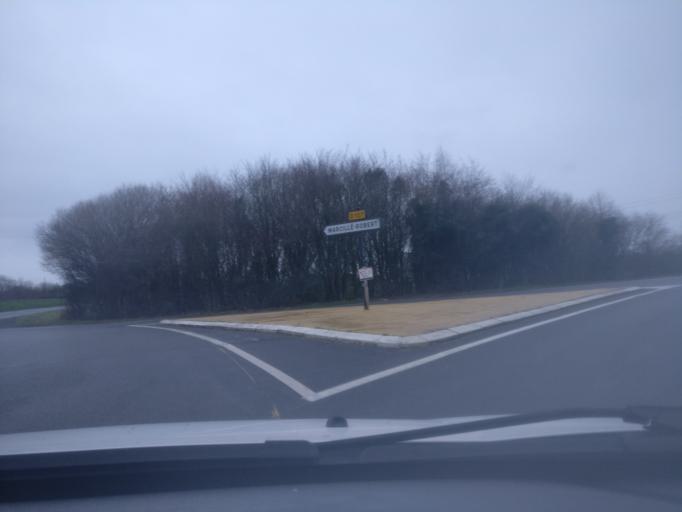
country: FR
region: Brittany
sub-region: Departement d'Ille-et-Vilaine
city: Louvigne-de-Bais
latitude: 48.0295
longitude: -1.3156
